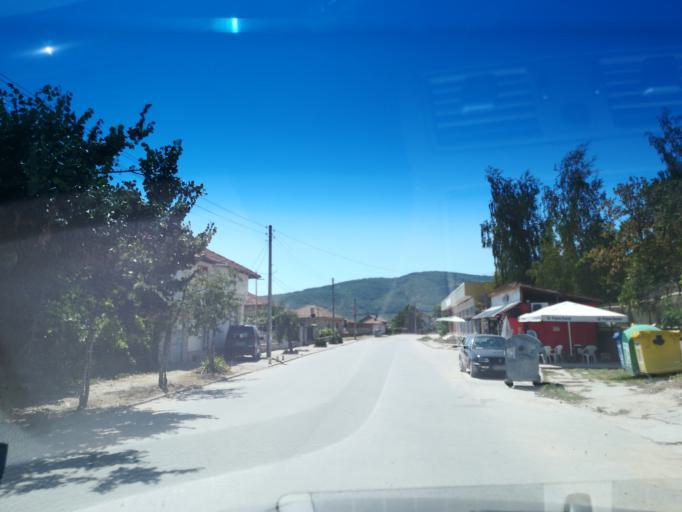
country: BG
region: Pazardzhik
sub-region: Obshtina Strelcha
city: Strelcha
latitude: 42.5018
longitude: 24.3212
